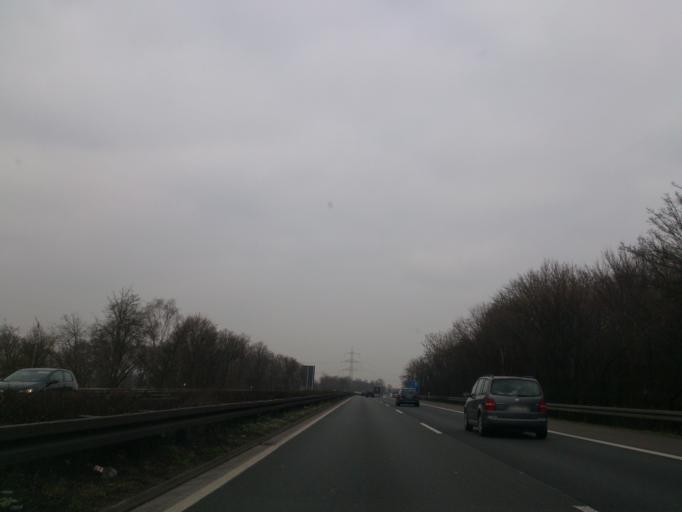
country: DE
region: North Rhine-Westphalia
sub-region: Regierungsbezirk Dusseldorf
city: Viersen
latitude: 51.2165
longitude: 6.3974
